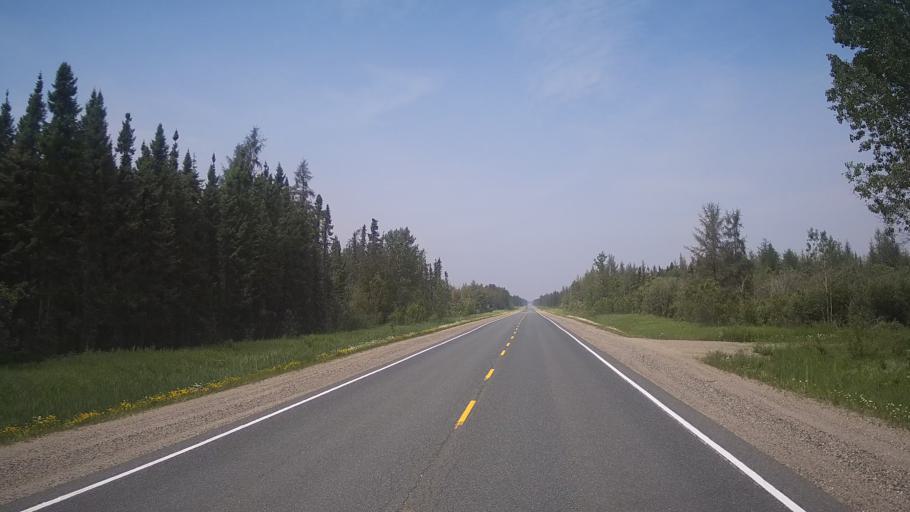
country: CA
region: Ontario
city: Timmins
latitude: 48.8272
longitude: -81.3715
